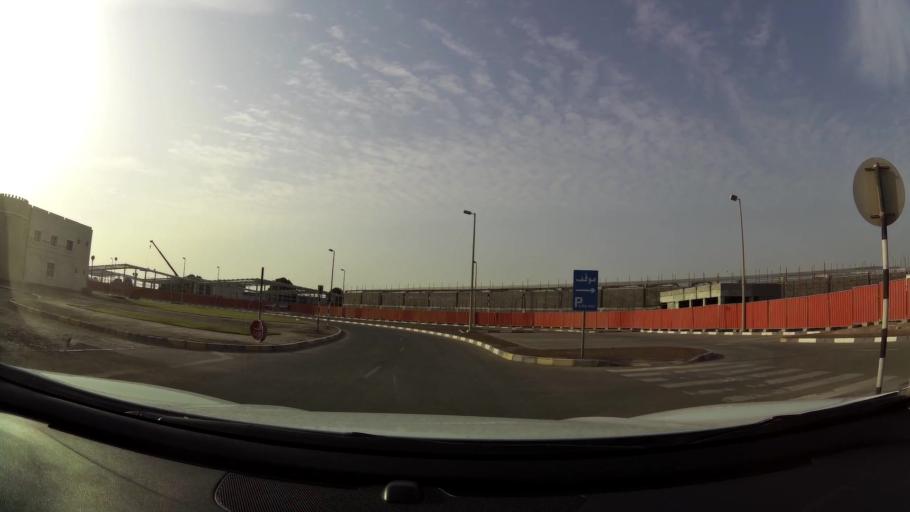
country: AE
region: Abu Dhabi
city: Abu Dhabi
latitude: 24.3301
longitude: 54.5212
